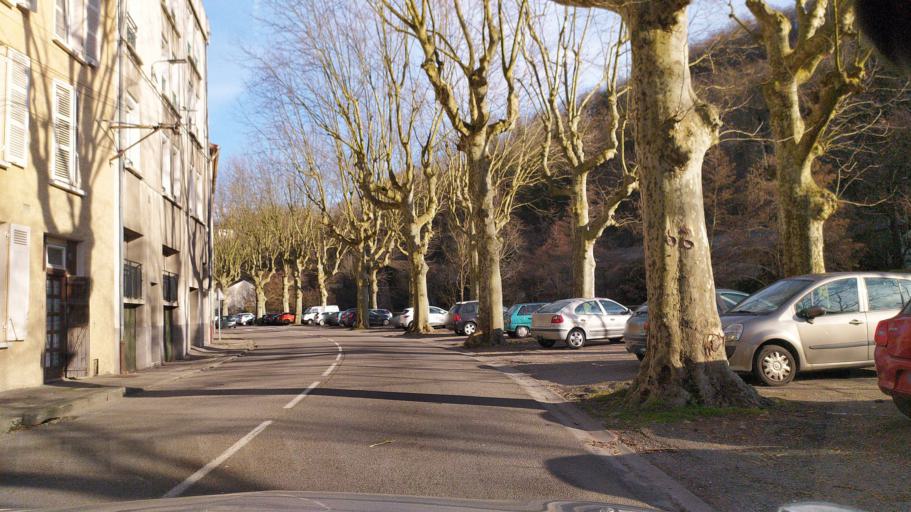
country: FR
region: Rhone-Alpes
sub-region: Departement de l'Isere
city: Pont-Eveque
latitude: 45.5270
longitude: 4.8957
